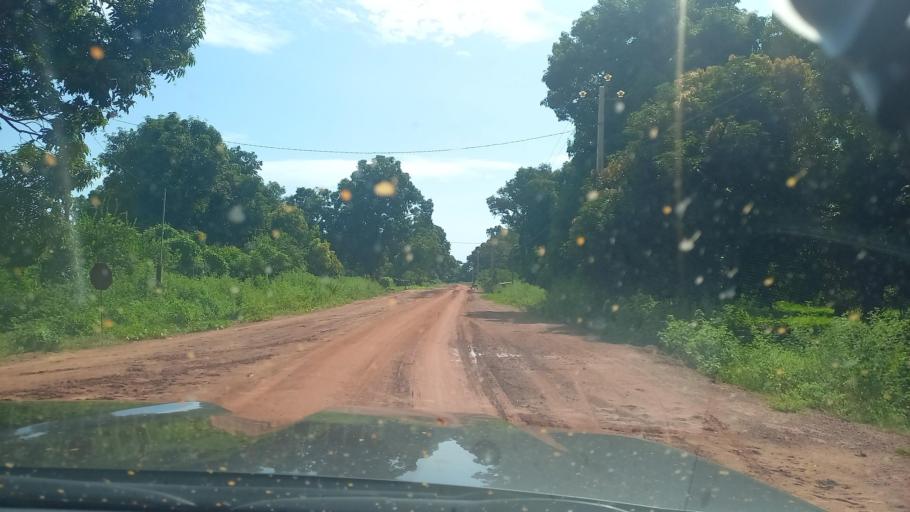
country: SN
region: Ziguinchor
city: Adeane
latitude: 12.6641
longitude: -16.1098
